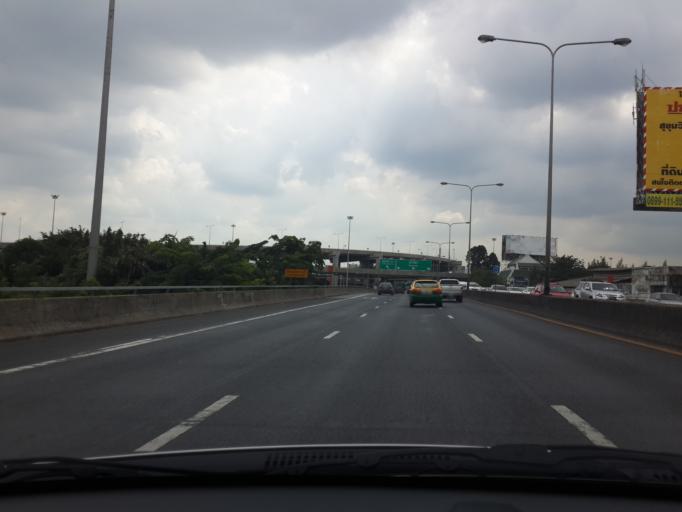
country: TH
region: Bangkok
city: Phra Khanong
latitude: 13.7033
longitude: 100.5898
